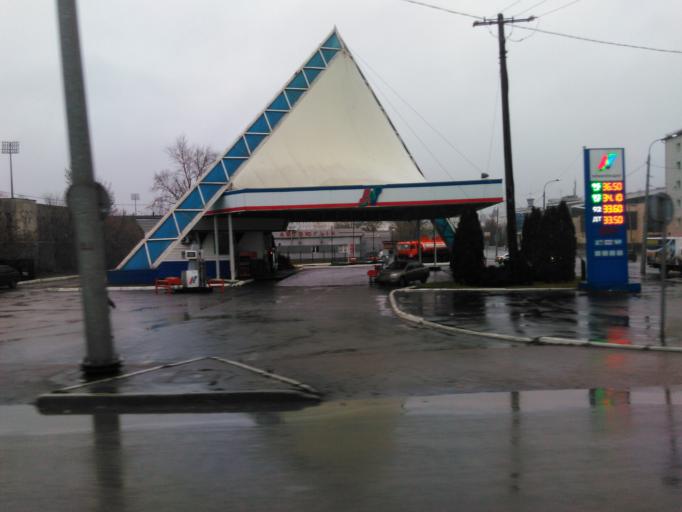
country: RU
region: Tatarstan
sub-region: Gorod Kazan'
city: Kazan
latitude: 55.7940
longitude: 49.0961
